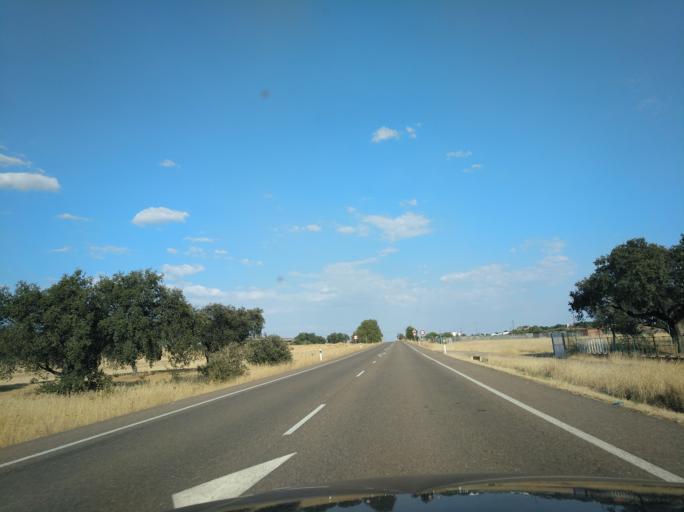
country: ES
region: Extremadura
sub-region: Provincia de Badajoz
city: Villanueva del Fresno
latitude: 38.3775
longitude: -7.1837
